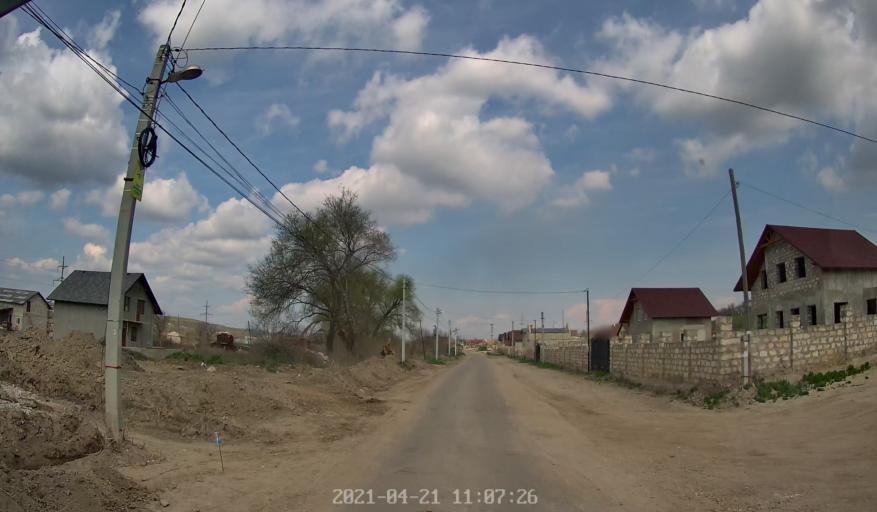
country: MD
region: Chisinau
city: Singera
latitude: 46.9489
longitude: 28.9455
